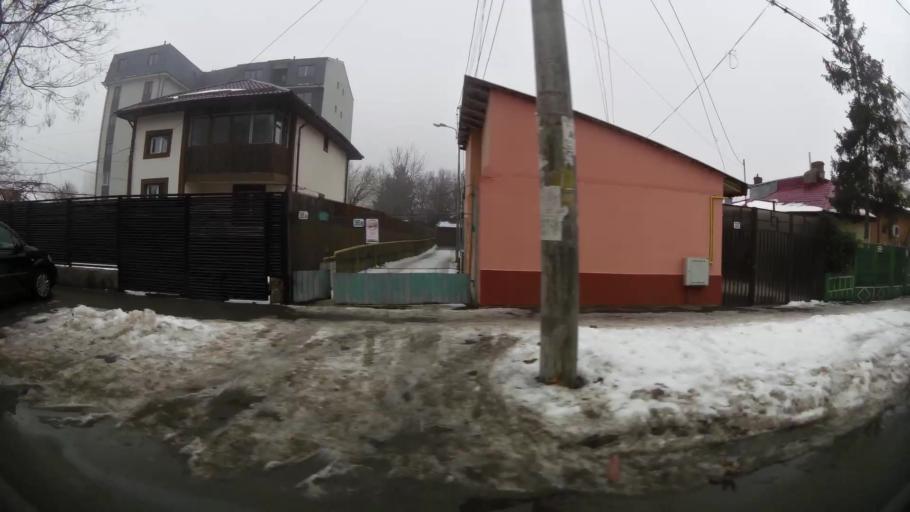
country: RO
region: Ilfov
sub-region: Comuna Chiajna
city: Rosu
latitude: 44.4699
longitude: 26.0208
